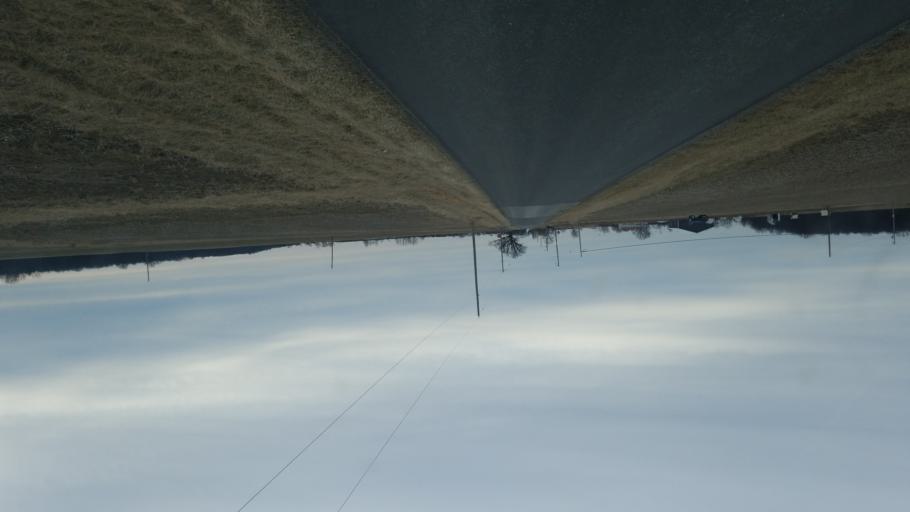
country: US
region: Ohio
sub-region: Defiance County
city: Hicksville
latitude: 41.3549
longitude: -84.7864
